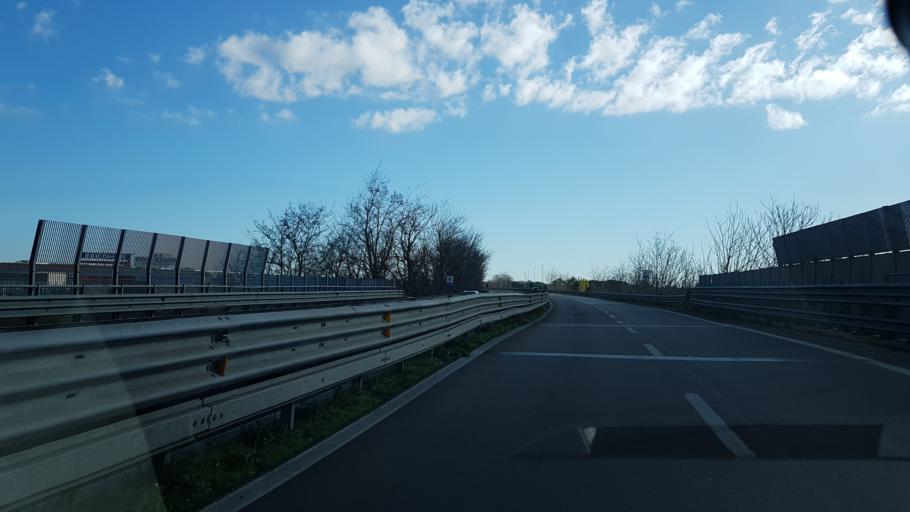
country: IT
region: Apulia
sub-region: Provincia di Lecce
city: Castromediano
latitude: 40.3235
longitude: 18.1715
